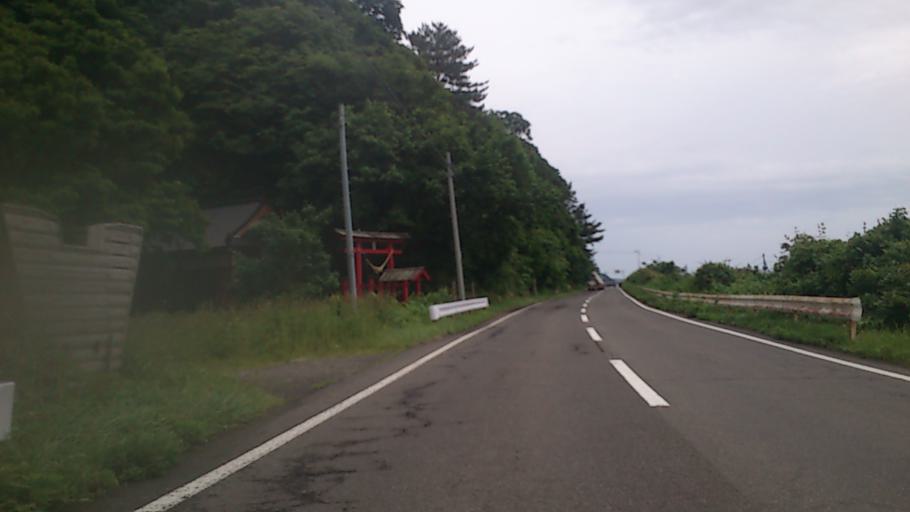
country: JP
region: Akita
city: Noshiromachi
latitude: 40.5160
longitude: 139.9512
